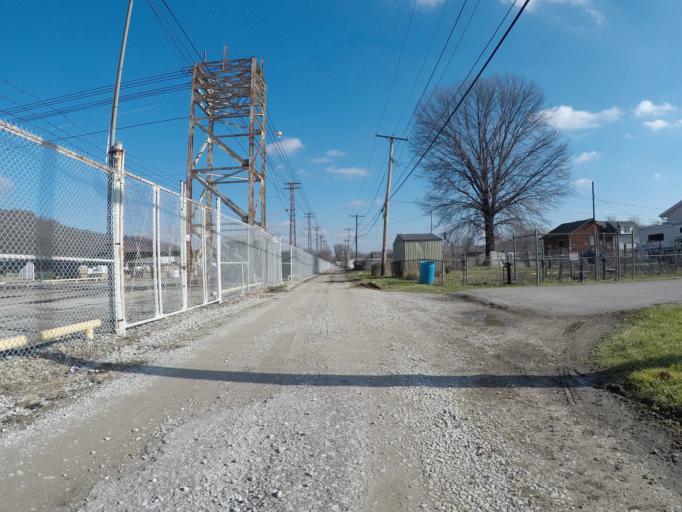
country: US
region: West Virginia
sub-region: Cabell County
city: Pea Ridge
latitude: 38.4142
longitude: -82.3786
